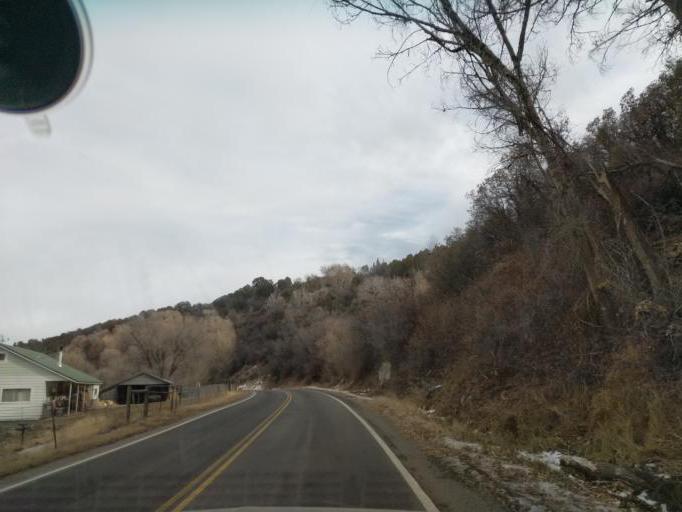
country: US
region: Colorado
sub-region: Mesa County
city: Palisade
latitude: 39.1871
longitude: -108.1383
